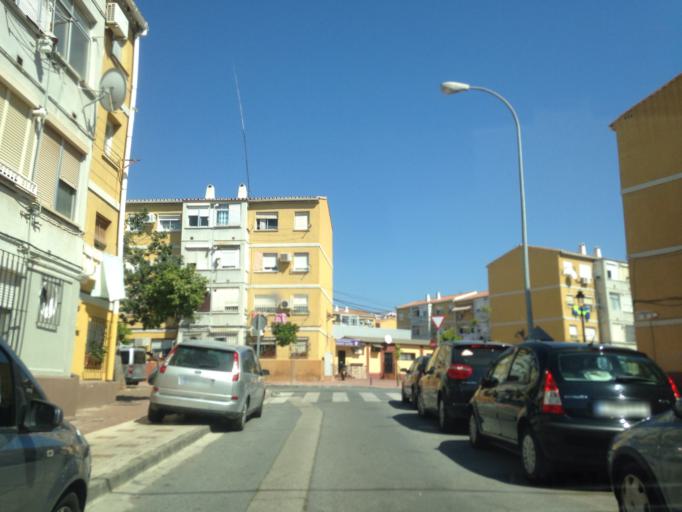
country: ES
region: Andalusia
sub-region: Provincia de Malaga
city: Malaga
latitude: 36.7166
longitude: -4.4526
